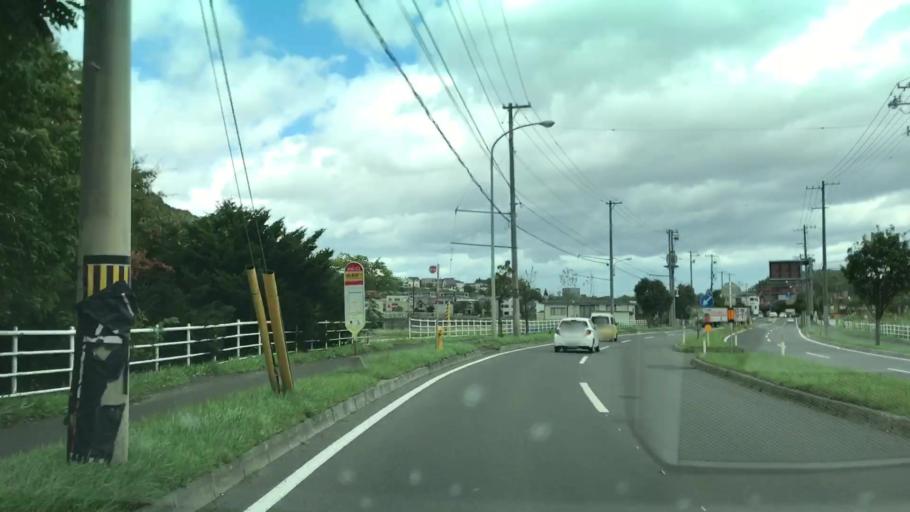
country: JP
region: Hokkaido
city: Sapporo
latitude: 42.9796
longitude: 141.4388
